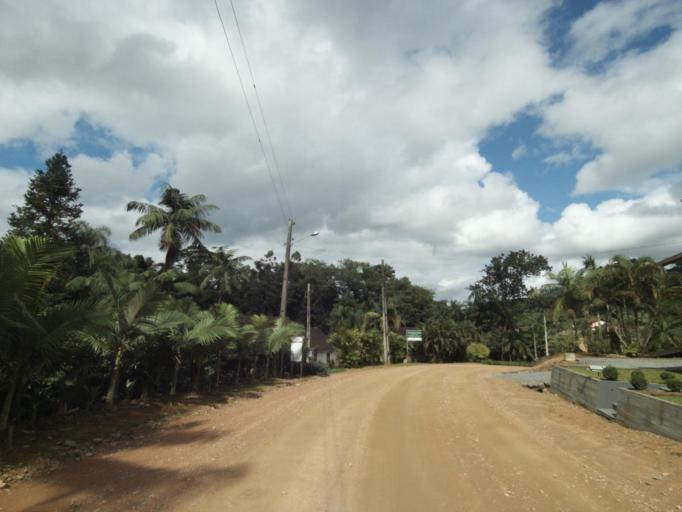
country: BR
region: Santa Catarina
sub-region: Pomerode
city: Pomerode
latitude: -26.6939
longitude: -49.1752
